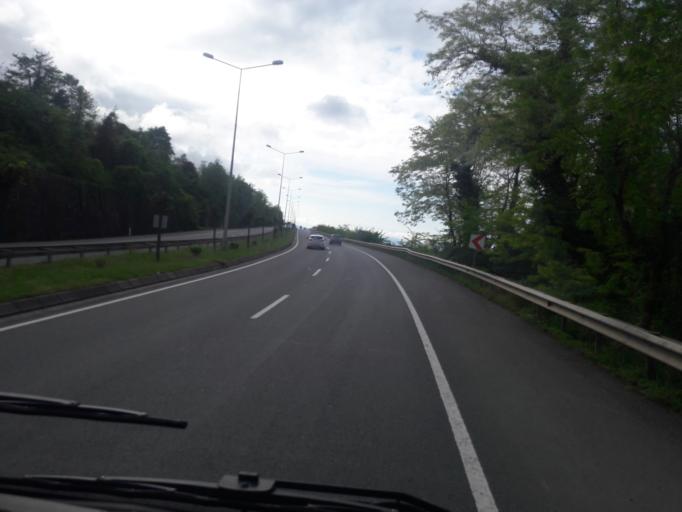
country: TR
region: Giresun
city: Piraziz
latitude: 40.9612
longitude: 38.1036
